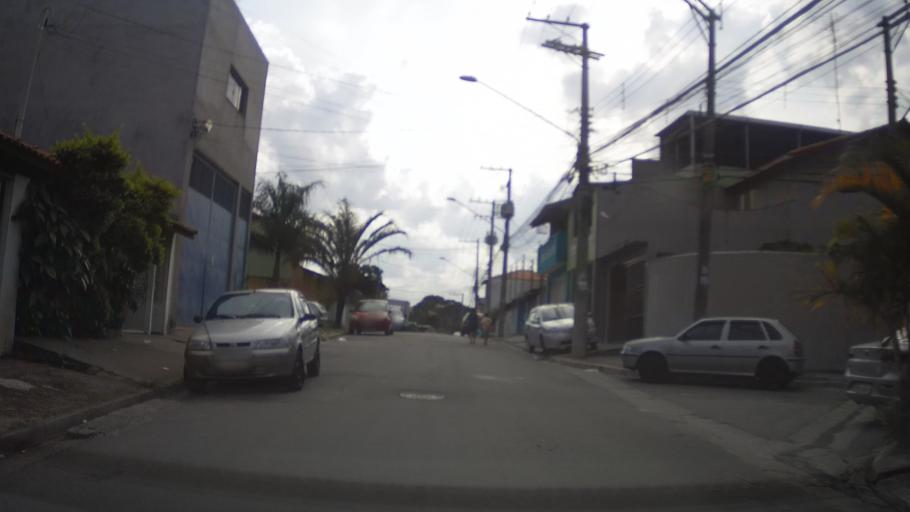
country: BR
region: Sao Paulo
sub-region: Guarulhos
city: Guarulhos
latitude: -23.4576
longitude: -46.5029
